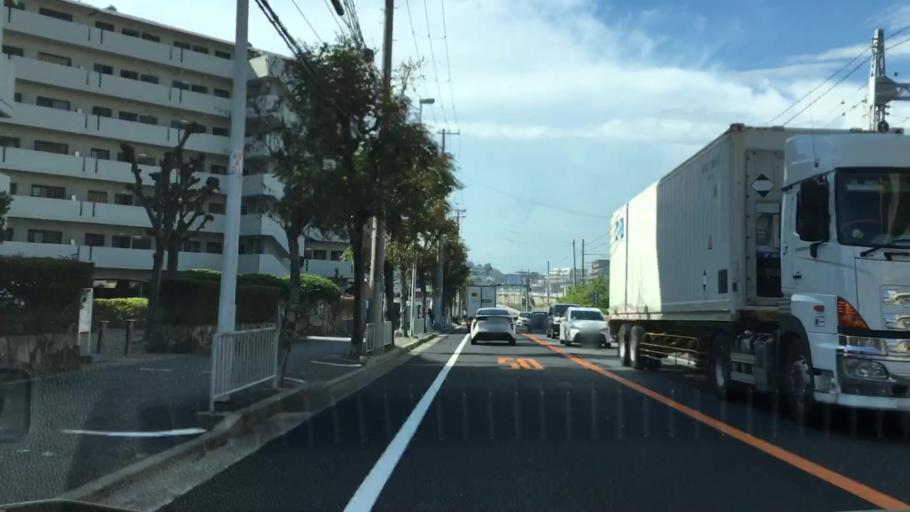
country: JP
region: Hyogo
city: Akashi
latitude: 34.6347
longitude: 135.0315
